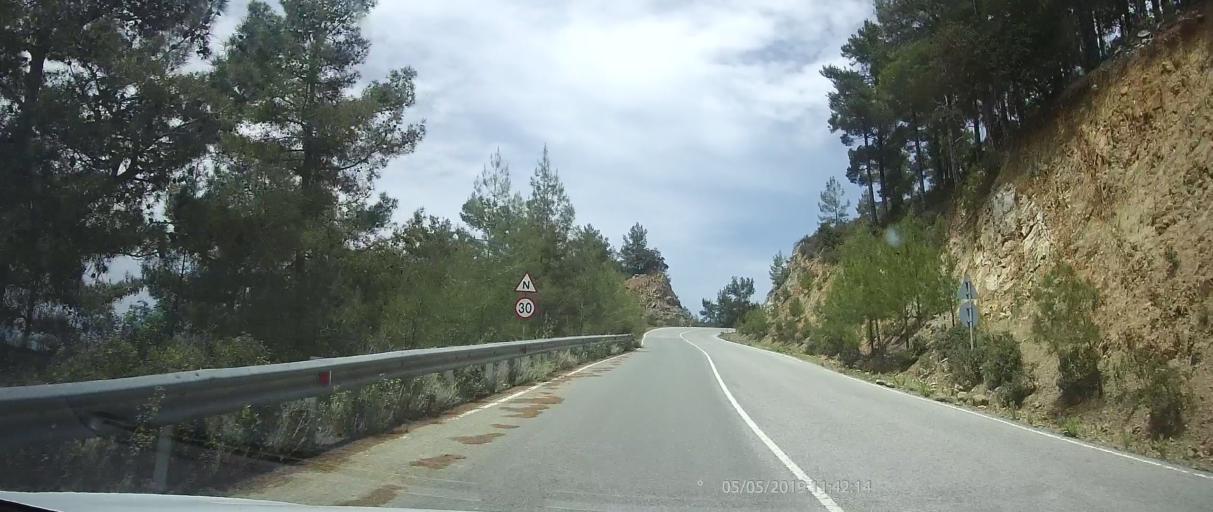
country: CY
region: Lefkosia
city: Kato Pyrgos
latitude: 35.0007
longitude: 32.6715
